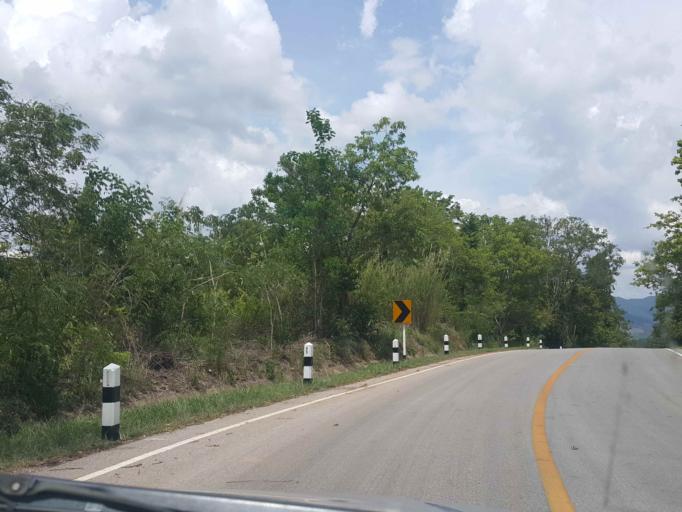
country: TH
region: Nan
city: Ban Luang
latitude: 18.8455
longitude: 100.4031
